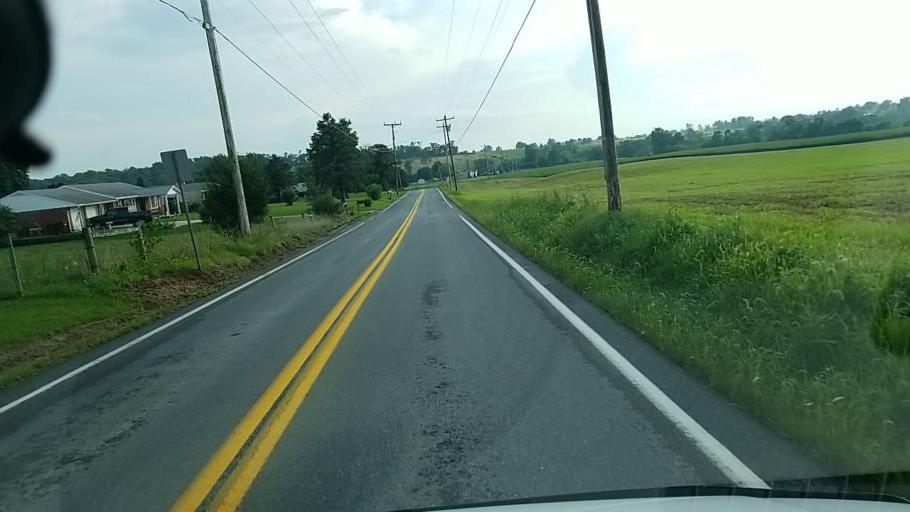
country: US
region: Pennsylvania
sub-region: Cumberland County
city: Newville
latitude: 40.2194
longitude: -77.4631
